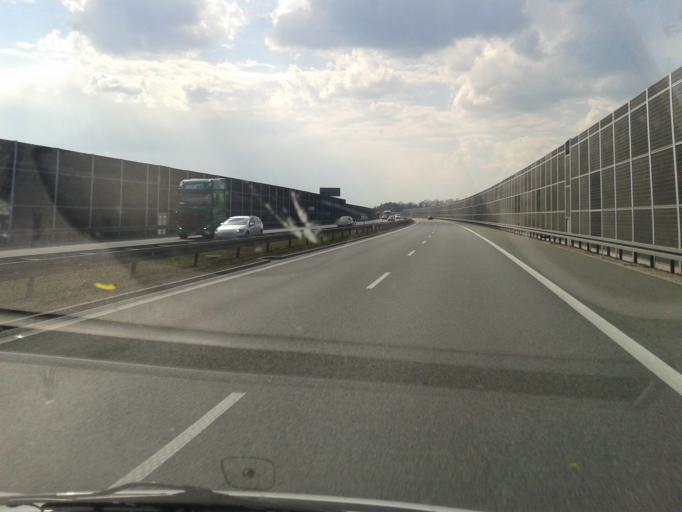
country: PL
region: Lesser Poland Voivodeship
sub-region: Powiat bochenski
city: Bochnia
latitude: 50.0050
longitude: 20.4147
